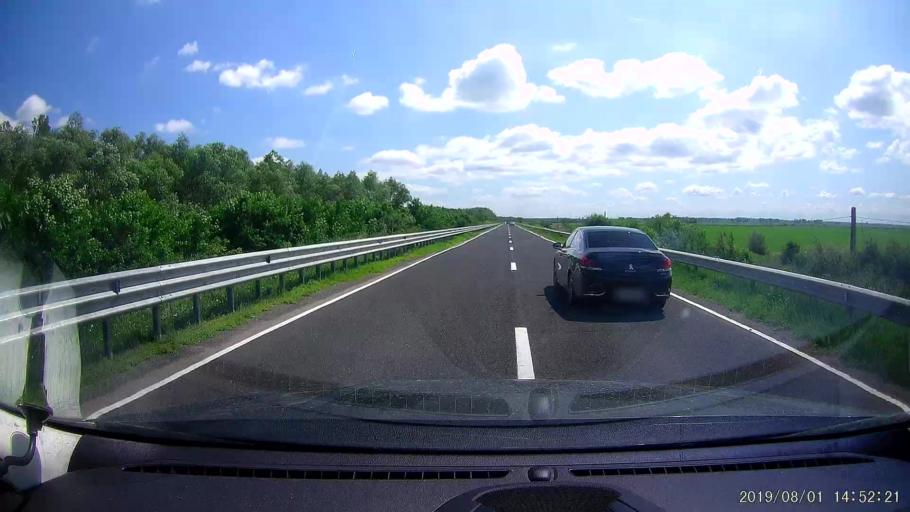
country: RO
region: Braila
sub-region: Comuna Vadeni
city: Vadeni
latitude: 45.3569
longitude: 28.0112
